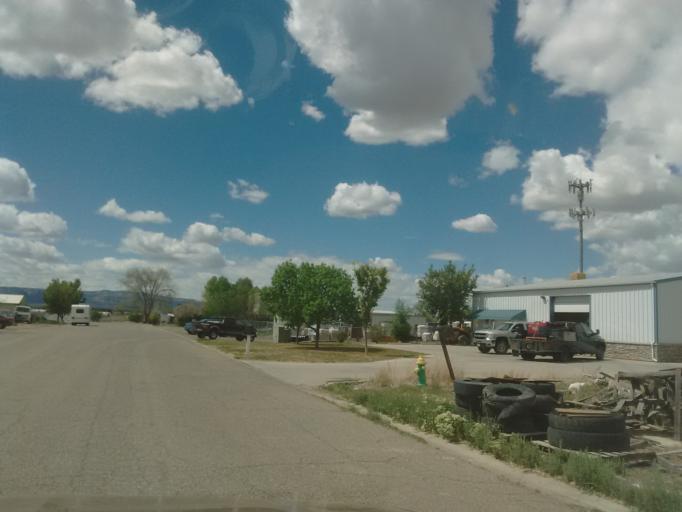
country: US
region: Colorado
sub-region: Mesa County
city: Fruitvale
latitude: 39.0728
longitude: -108.4987
